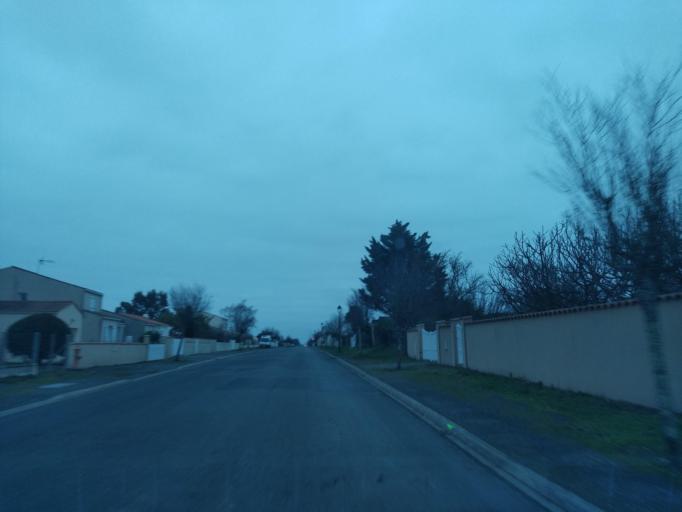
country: FR
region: Pays de la Loire
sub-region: Departement de la Vendee
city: Triaize
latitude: 46.3526
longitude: -1.2586
